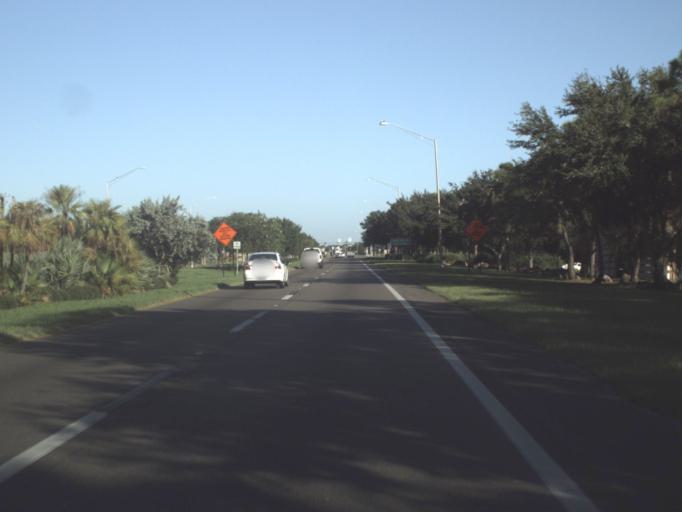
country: US
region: Florida
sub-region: Lee County
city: North Fort Myers
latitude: 26.6565
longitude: -81.8815
